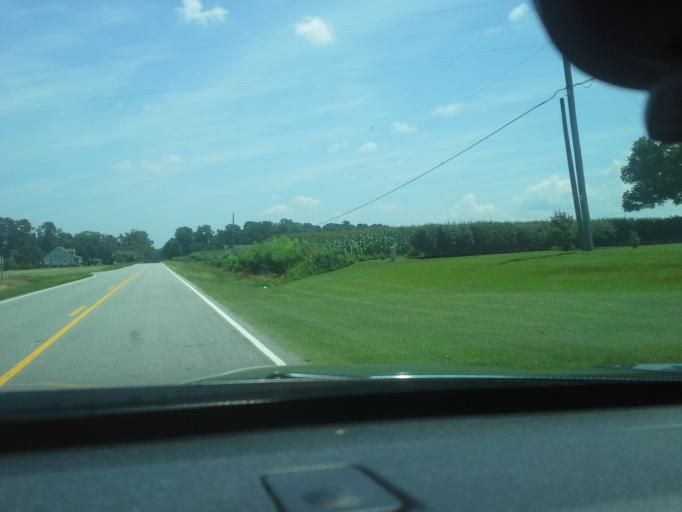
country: US
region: North Carolina
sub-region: Washington County
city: Plymouth
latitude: 35.9077
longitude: -76.6642
